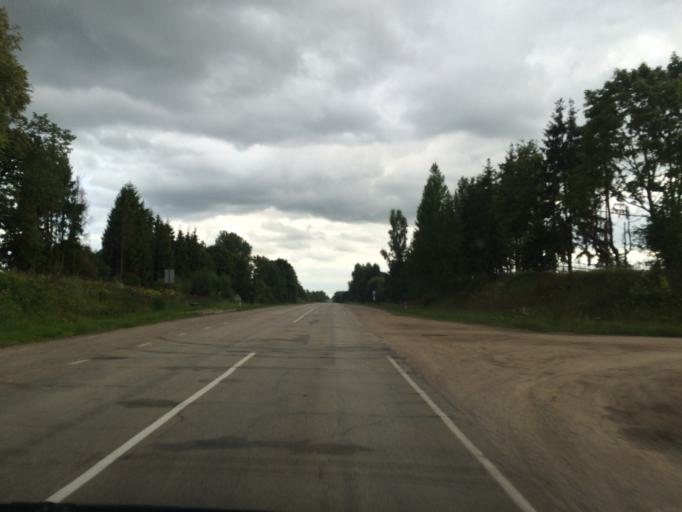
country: LV
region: Rezekne
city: Rezekne
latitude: 56.5607
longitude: 27.3640
